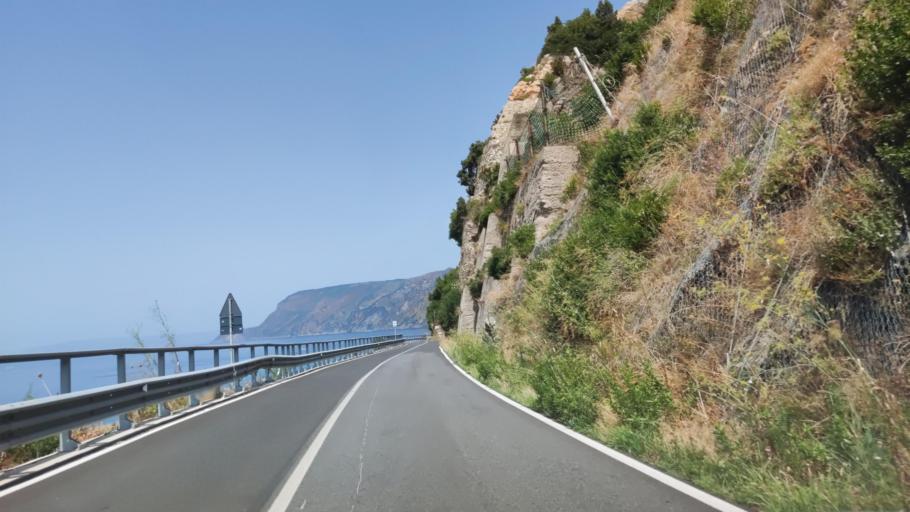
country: IT
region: Calabria
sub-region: Provincia di Reggio Calabria
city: Bagnara Calabra
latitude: 38.2748
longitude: 15.7855
